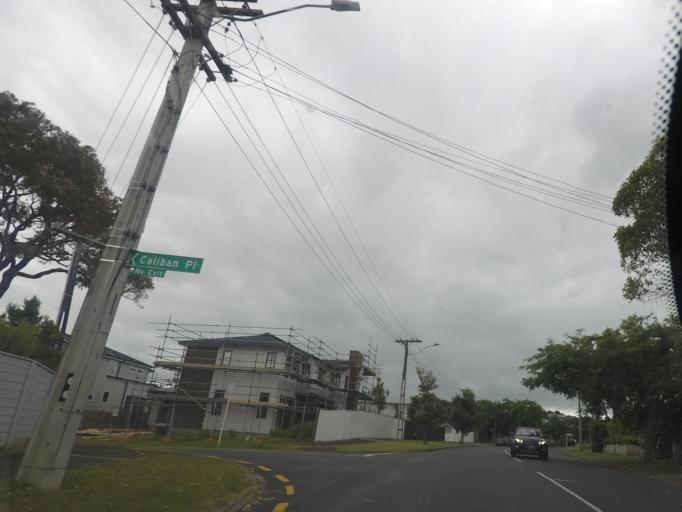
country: NZ
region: Auckland
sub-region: Auckland
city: Tamaki
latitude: -36.8663
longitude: 174.8586
